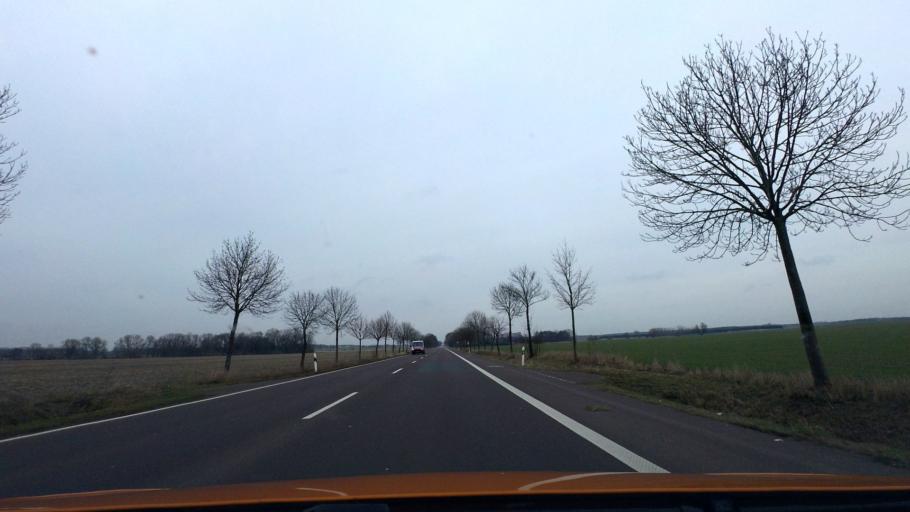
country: DE
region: Saxony-Anhalt
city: Gerwisch
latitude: 52.1840
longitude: 11.7589
